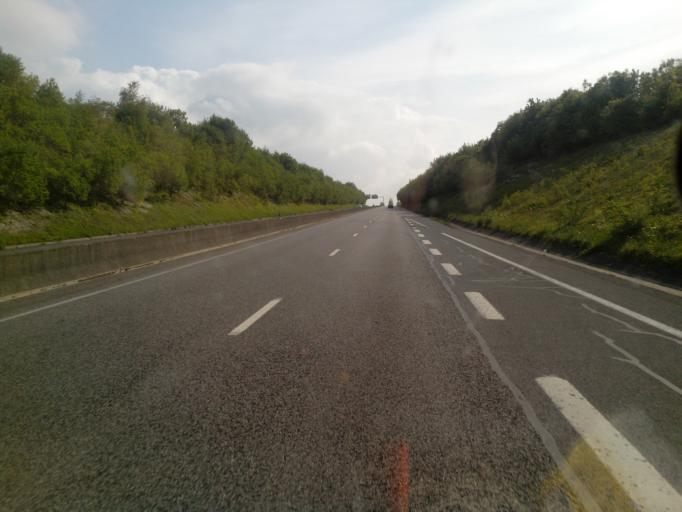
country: FR
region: Haute-Normandie
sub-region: Departement de la Seine-Maritime
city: Neufchatel-en-Bray
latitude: 49.7507
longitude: 1.4806
